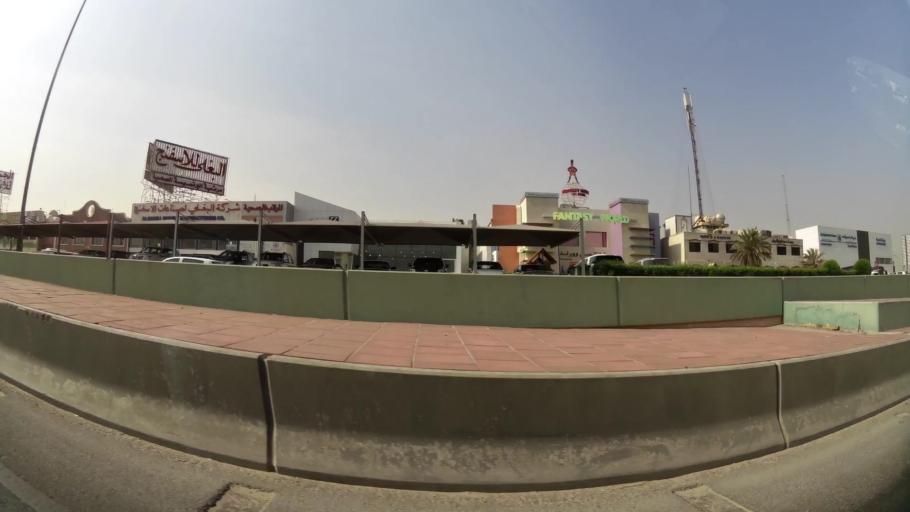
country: KW
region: Al Asimah
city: Ar Rabiyah
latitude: 29.3127
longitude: 47.9425
